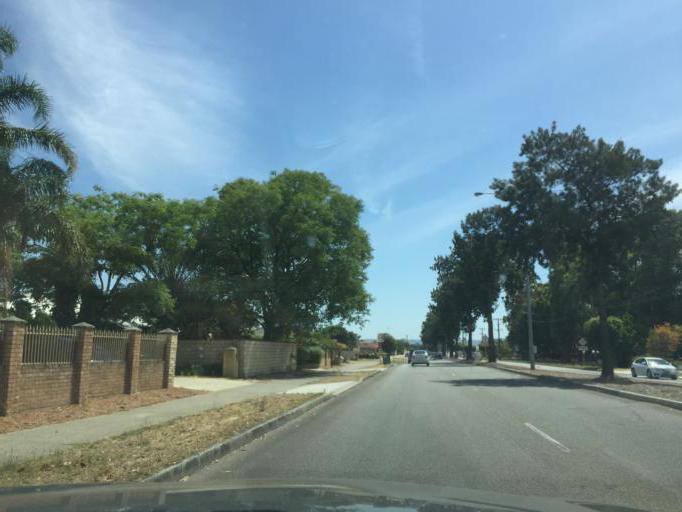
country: AU
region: Western Australia
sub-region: Gosnells
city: Thornlie
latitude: -32.0748
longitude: 115.9616
